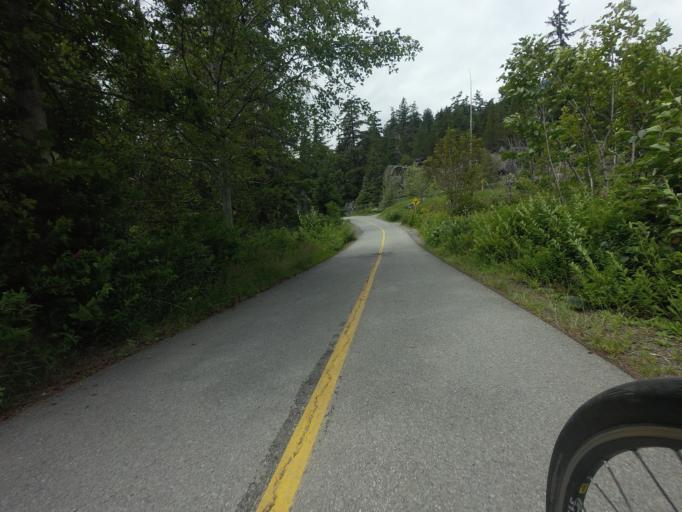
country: CA
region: British Columbia
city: Whistler
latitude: 50.1032
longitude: -122.9896
